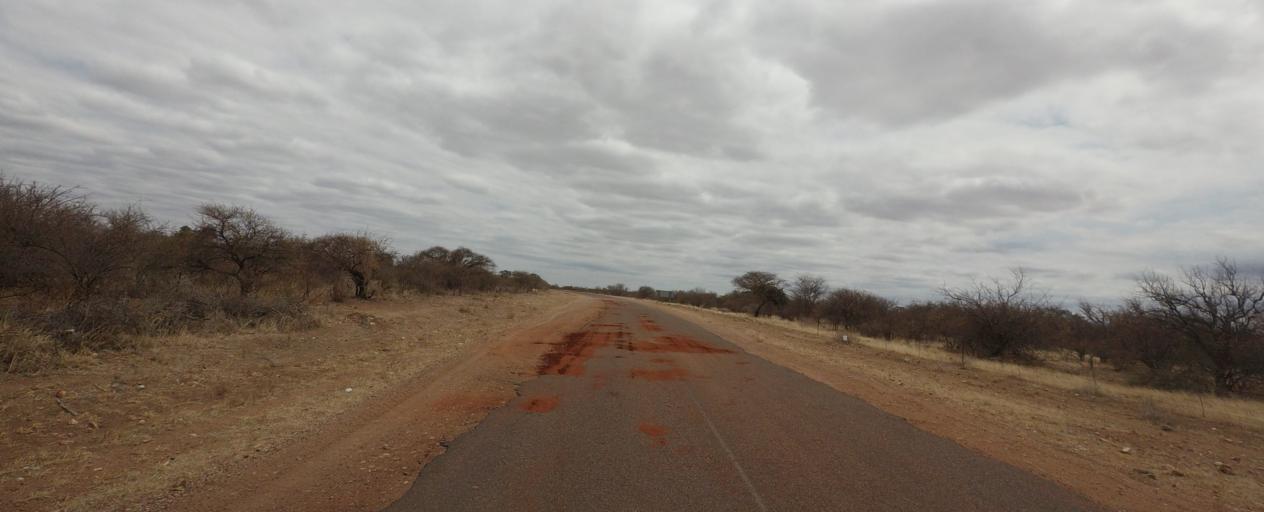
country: BW
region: Central
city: Makobeng
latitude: -22.8319
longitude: 28.2160
